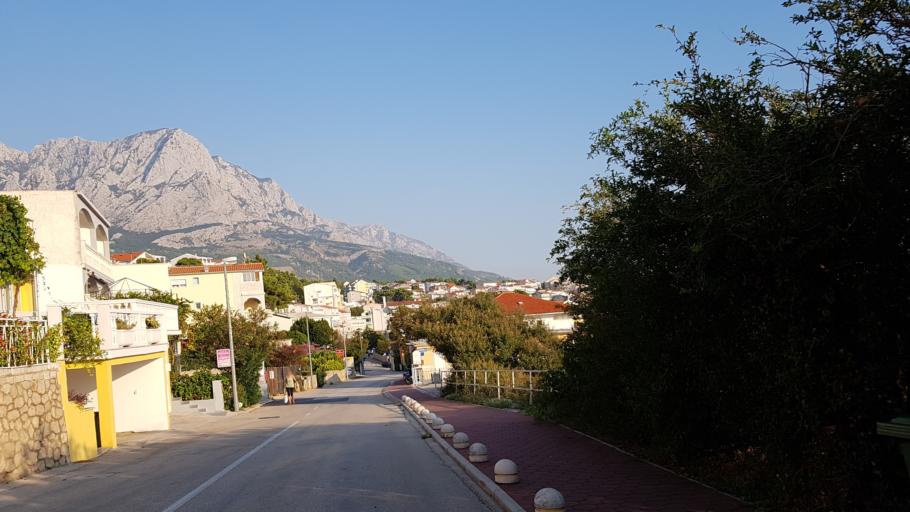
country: HR
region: Splitsko-Dalmatinska
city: Baska Voda
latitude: 43.3601
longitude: 16.9480
